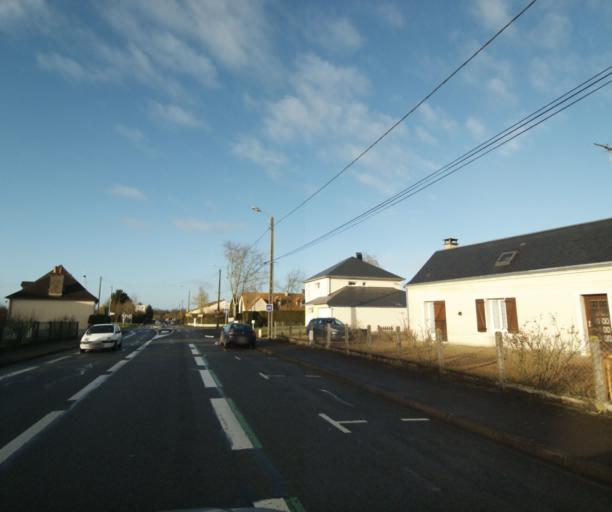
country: FR
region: Pays de la Loire
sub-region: Departement de la Sarthe
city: Sarge-les-le-Mans
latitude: 48.0158
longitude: 0.2317
